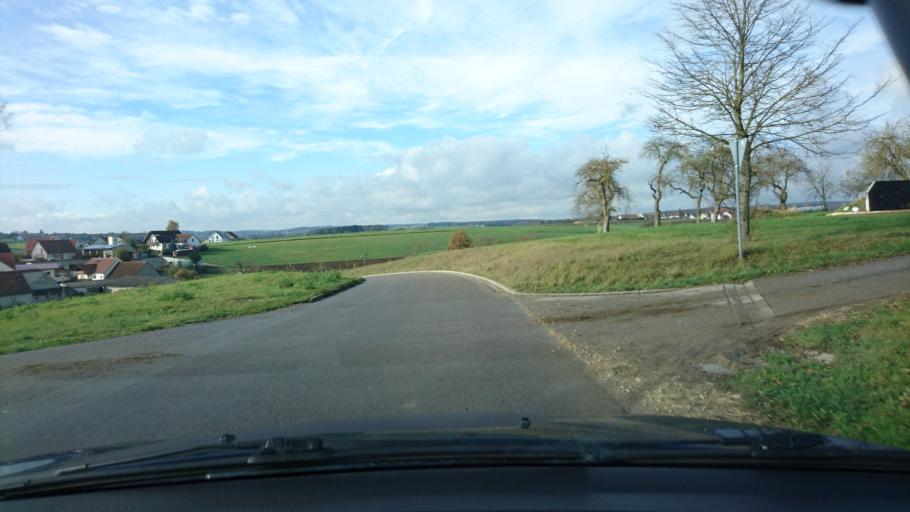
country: DE
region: Bavaria
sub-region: Swabia
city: Hohenaltheim
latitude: 48.7287
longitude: 10.5389
